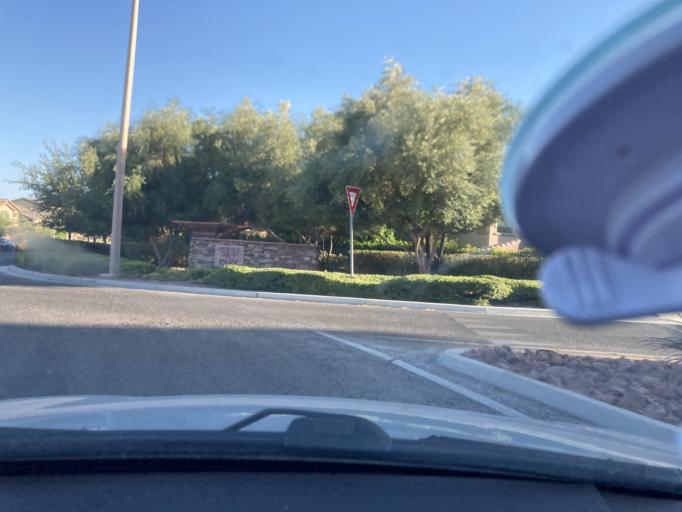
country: US
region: Nevada
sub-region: Clark County
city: Summerlin South
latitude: 36.1564
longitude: -115.3444
